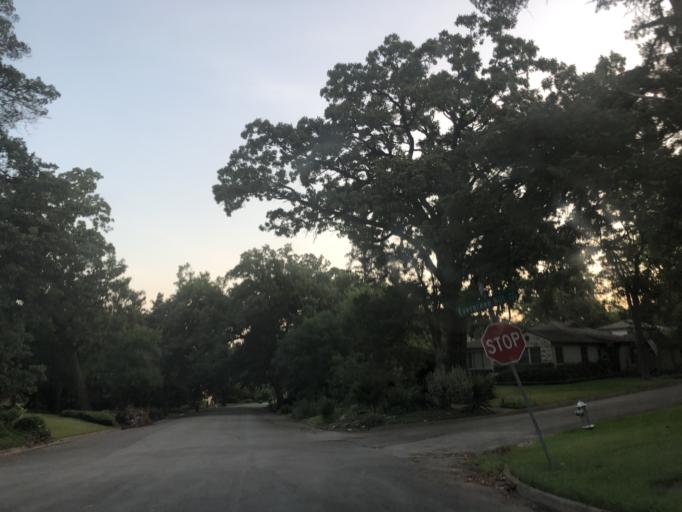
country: US
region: Texas
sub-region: Dallas County
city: Dallas
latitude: 32.7642
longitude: -96.8342
